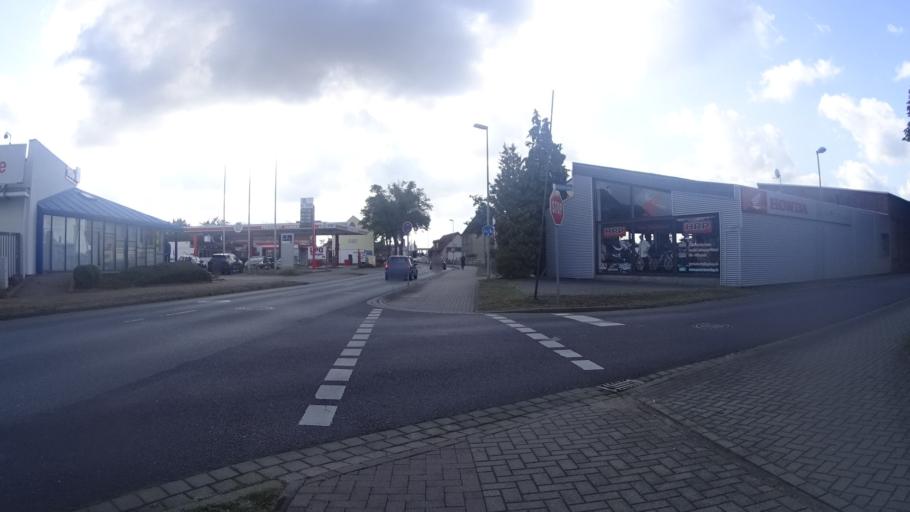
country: DE
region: Brandenburg
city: Wittenberge
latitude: 52.9982
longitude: 11.7344
